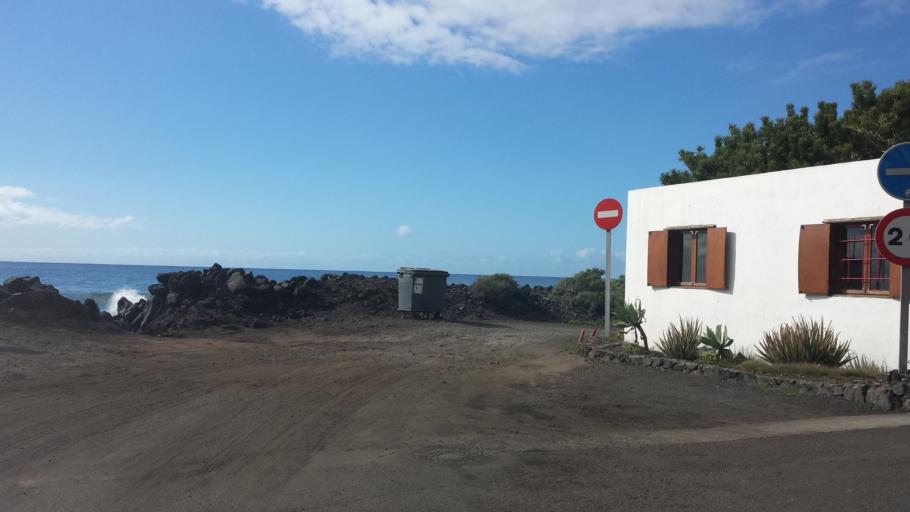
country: ES
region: Canary Islands
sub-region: Provincia de Santa Cruz de Tenerife
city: Fuencaliente de la Palma
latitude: 28.5518
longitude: -17.8879
